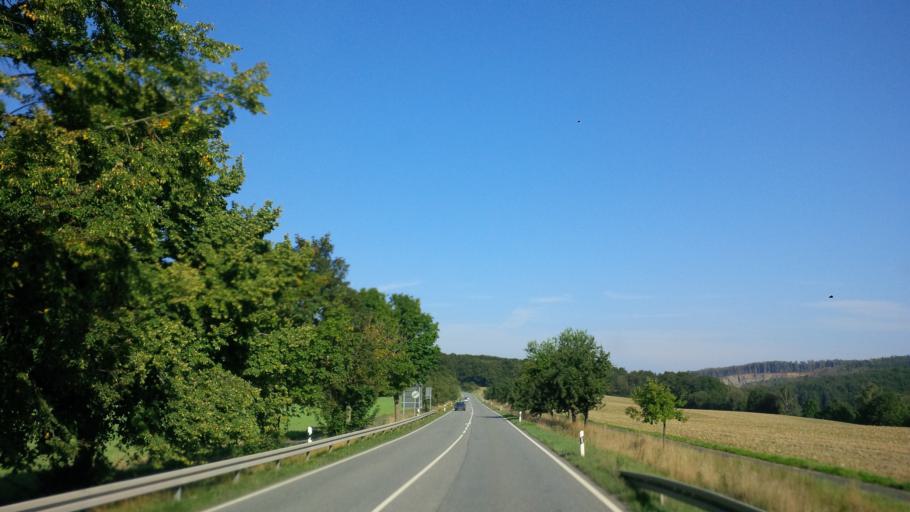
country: DE
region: Hesse
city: Weilmunster
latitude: 50.4541
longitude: 8.3904
